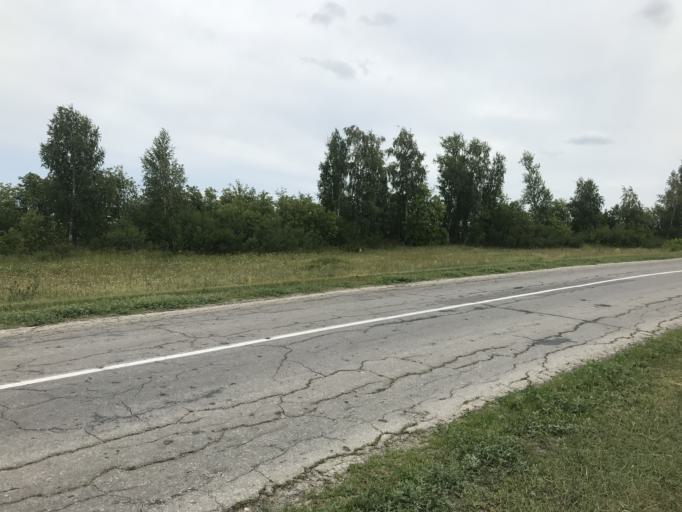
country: RU
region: Samara
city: Shigony
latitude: 53.6539
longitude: 48.8148
